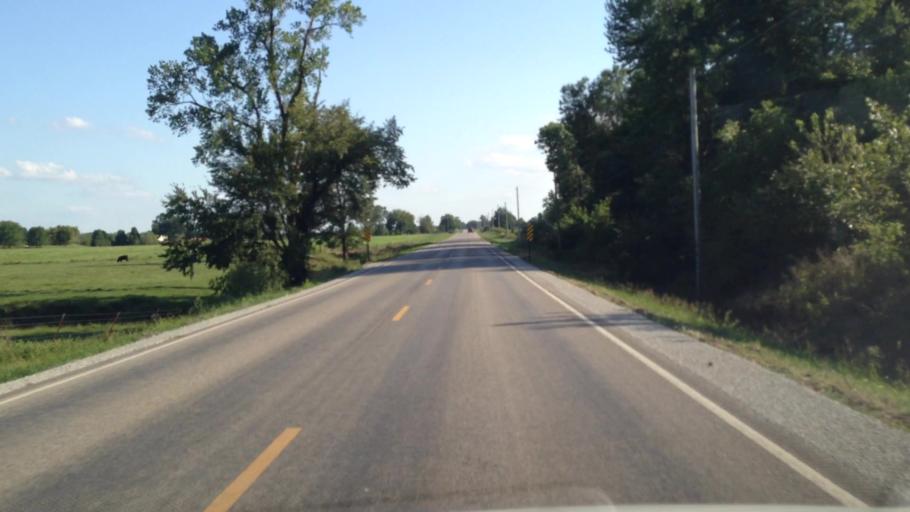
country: US
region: Kansas
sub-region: Crawford County
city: Pittsburg
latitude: 37.3507
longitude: -94.6315
